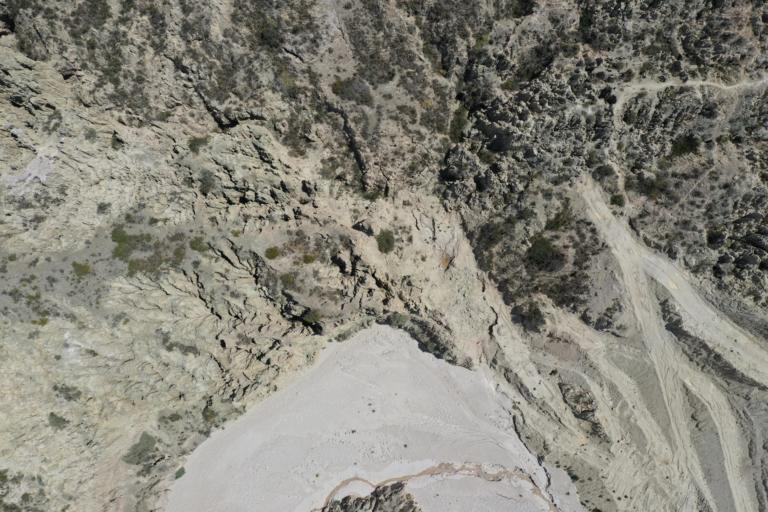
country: BO
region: La Paz
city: La Paz
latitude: -16.5616
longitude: -68.1122
